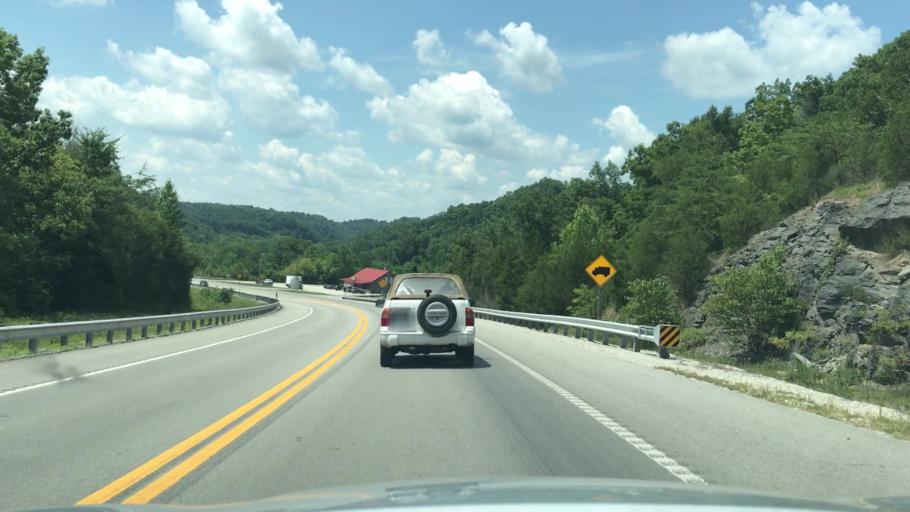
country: US
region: Tennessee
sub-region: Pickett County
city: Byrdstown
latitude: 36.6064
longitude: -85.1179
